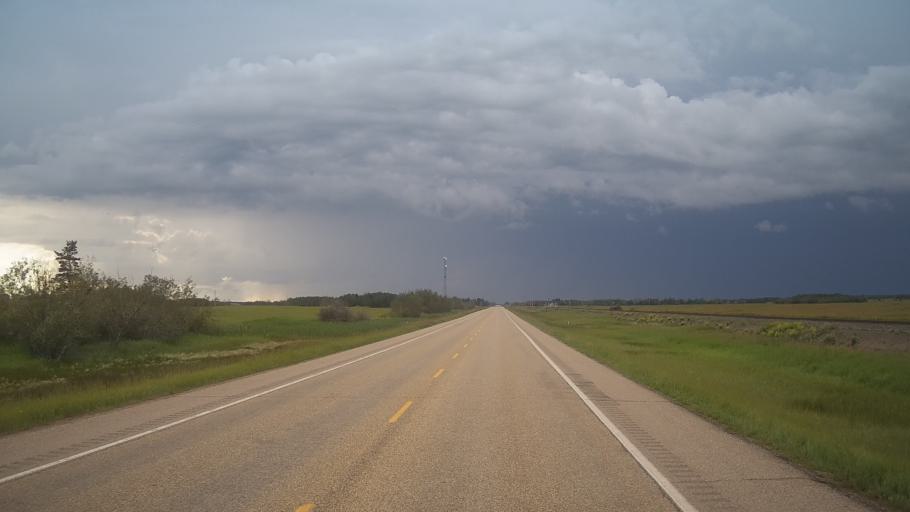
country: CA
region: Alberta
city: Tofield
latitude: 53.2661
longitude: -112.3574
